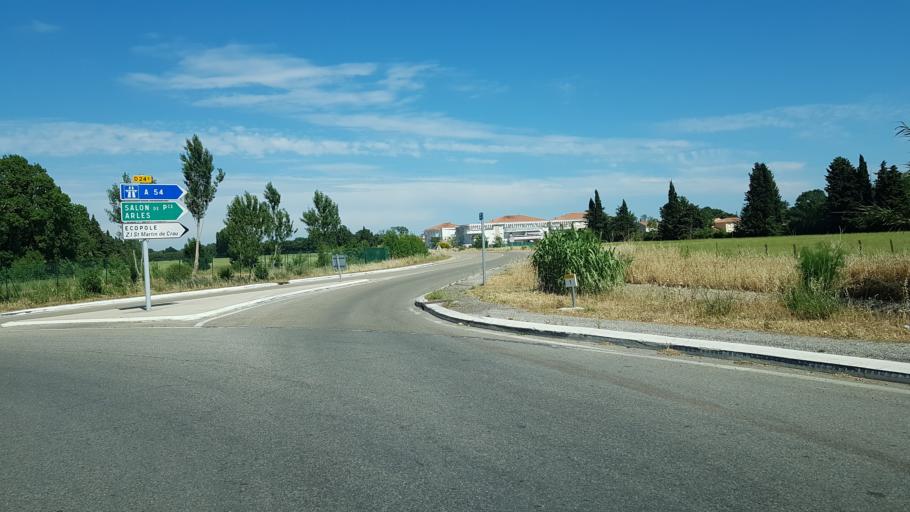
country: FR
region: Provence-Alpes-Cote d'Azur
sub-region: Departement des Bouches-du-Rhone
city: Saint-Martin-de-Crau
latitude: 43.6442
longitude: 4.8208
